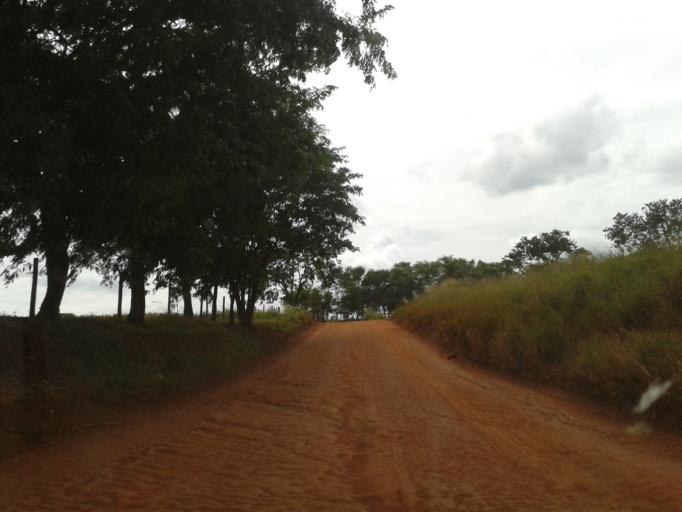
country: BR
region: Minas Gerais
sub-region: Centralina
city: Centralina
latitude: -18.7608
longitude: -49.2214
